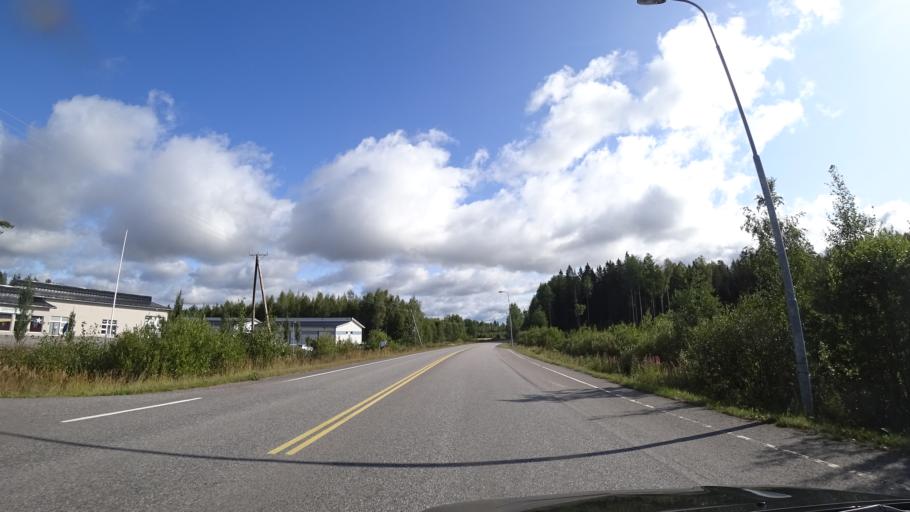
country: FI
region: Uusimaa
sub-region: Helsinki
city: Hyvinge
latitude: 60.5493
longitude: 24.9432
